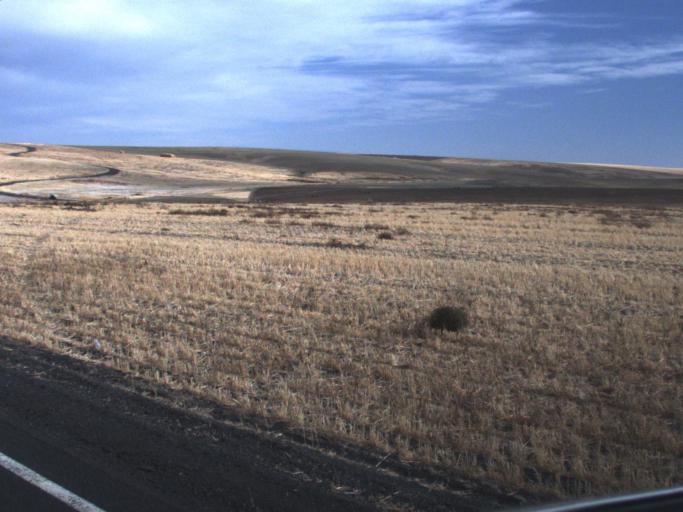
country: US
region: Washington
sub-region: Adams County
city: Ritzville
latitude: 47.3695
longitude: -118.6994
